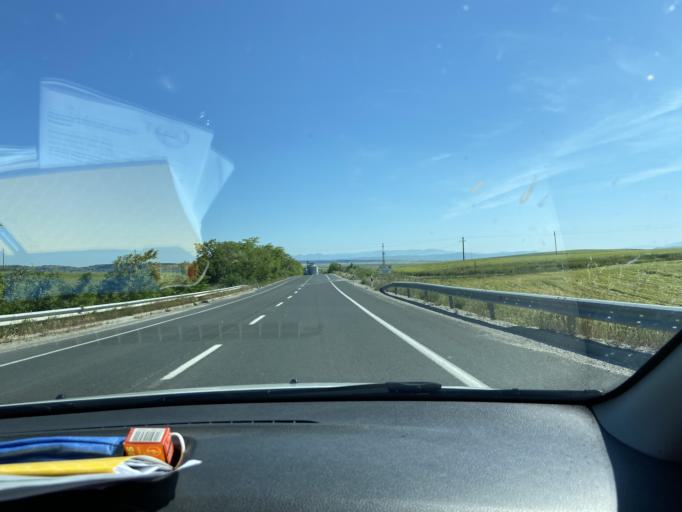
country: MK
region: Veles
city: Veles
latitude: 41.7589
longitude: 21.8298
